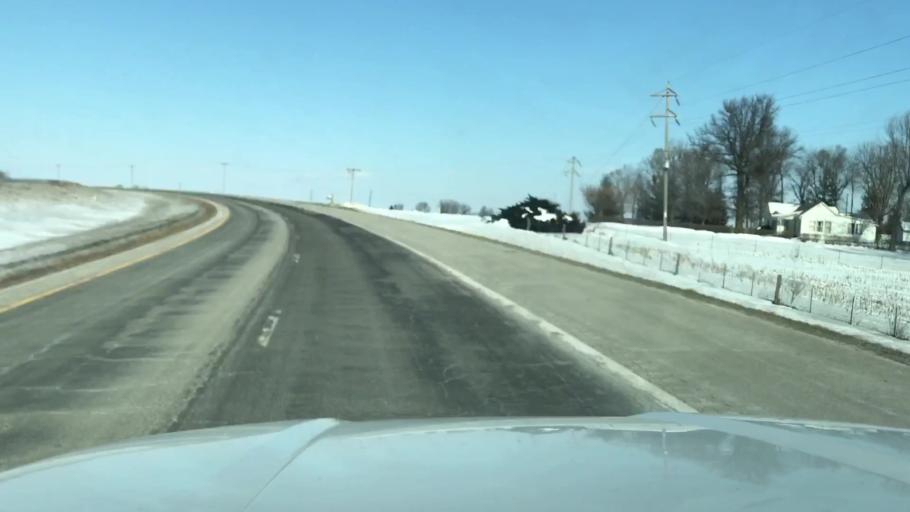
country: US
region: Missouri
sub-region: Nodaway County
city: Maryville
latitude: 40.2715
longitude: -94.8667
